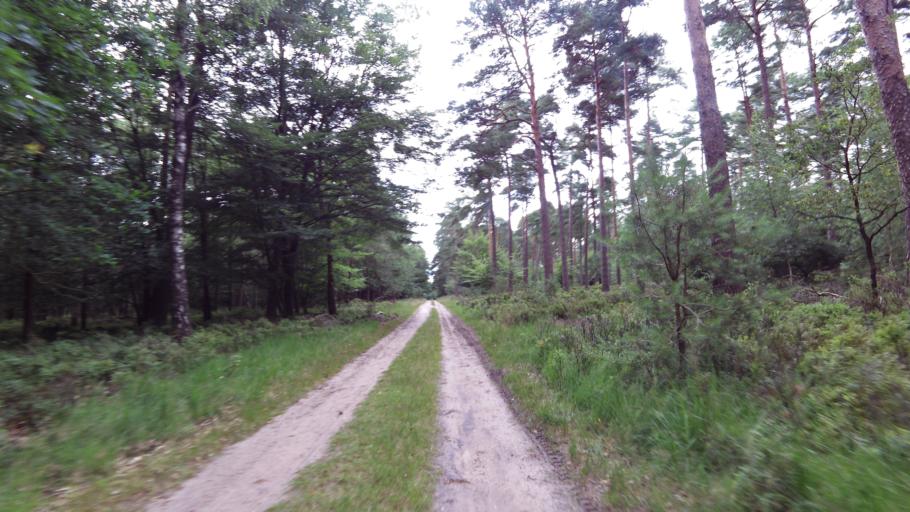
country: NL
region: Gelderland
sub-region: Gemeente Apeldoorn
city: Apeldoorn
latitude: 52.2060
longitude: 5.8920
